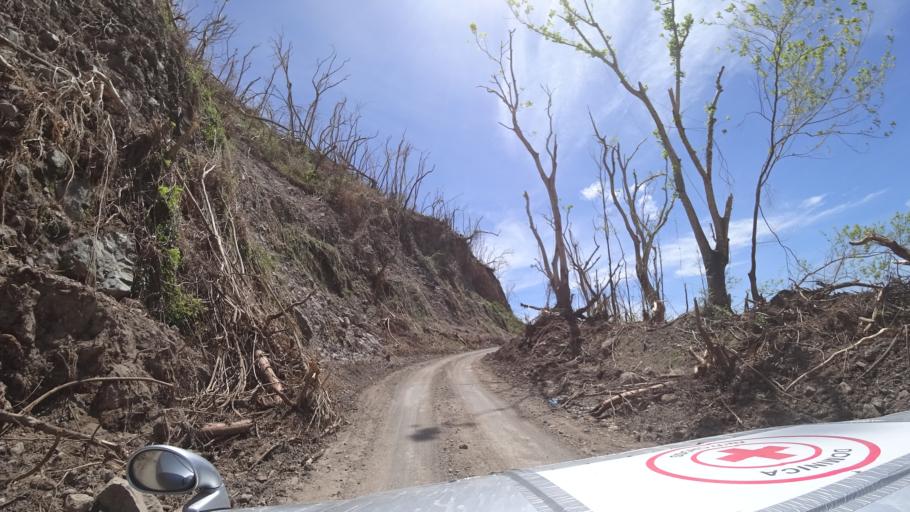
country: DM
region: Saint Mark
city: Soufriere
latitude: 15.2428
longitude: -61.3681
